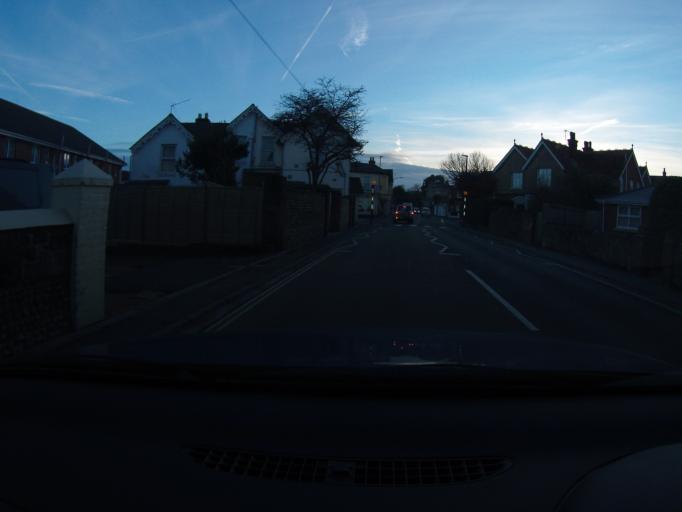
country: GB
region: England
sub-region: Isle of Wight
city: Sandown
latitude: 50.6565
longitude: -1.1581
